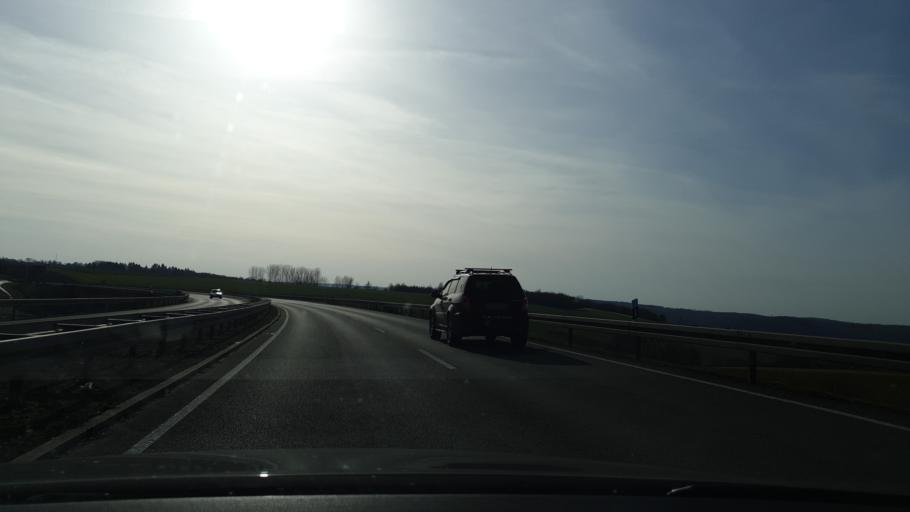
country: DE
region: Thuringia
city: Schwaara
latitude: 50.8942
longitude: 12.1145
